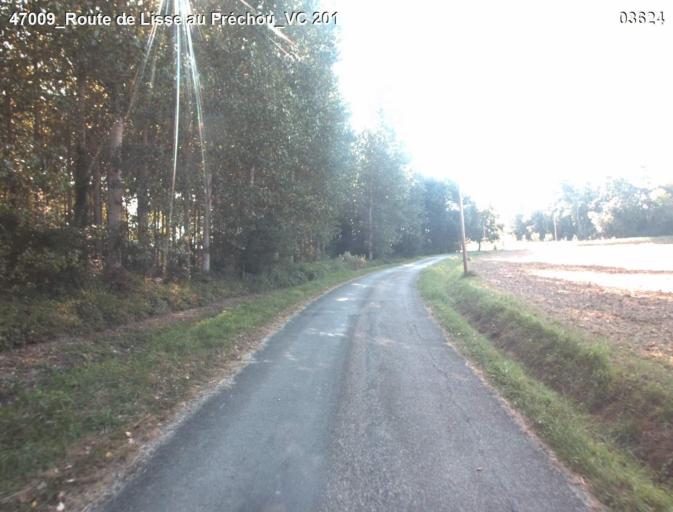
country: FR
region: Aquitaine
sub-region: Departement du Lot-et-Garonne
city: Mezin
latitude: 44.1014
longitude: 0.2752
